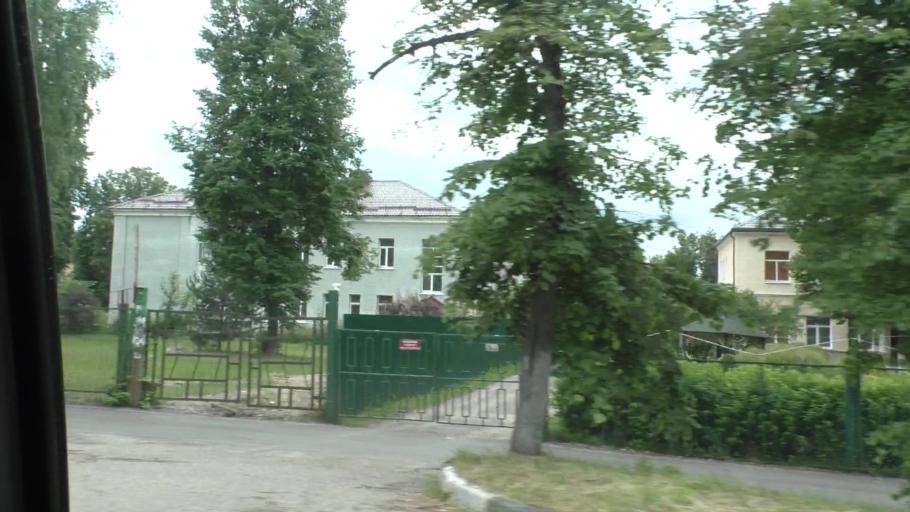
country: RU
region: Moskovskaya
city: Yegor'yevsk
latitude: 55.3911
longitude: 39.0237
